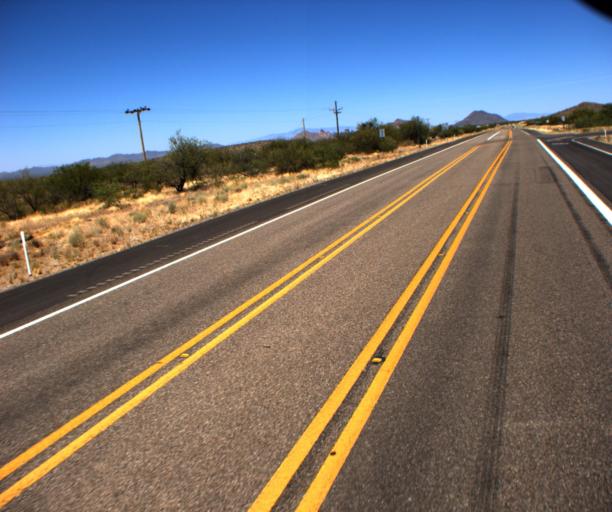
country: US
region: Arizona
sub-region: Pima County
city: Three Points
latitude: 32.0261
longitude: -111.5811
